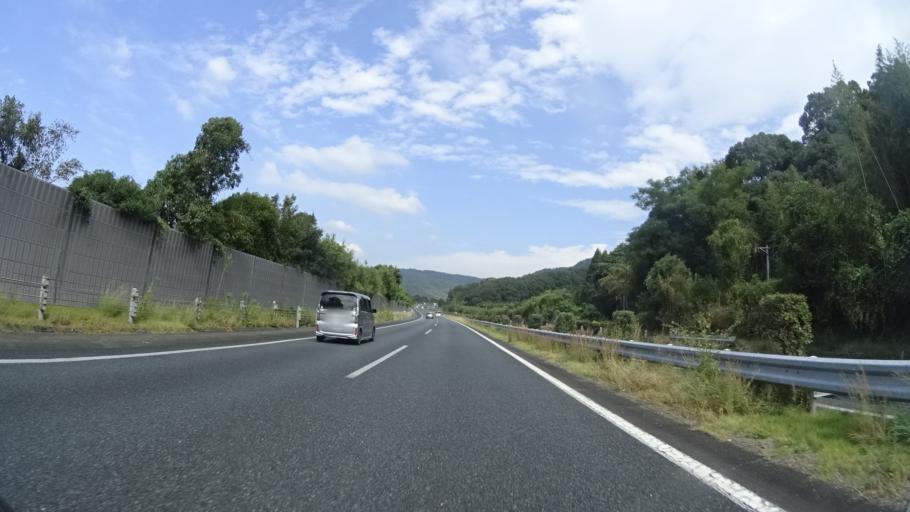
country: JP
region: Kumamoto
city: Matsubase
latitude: 32.5995
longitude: 130.7199
